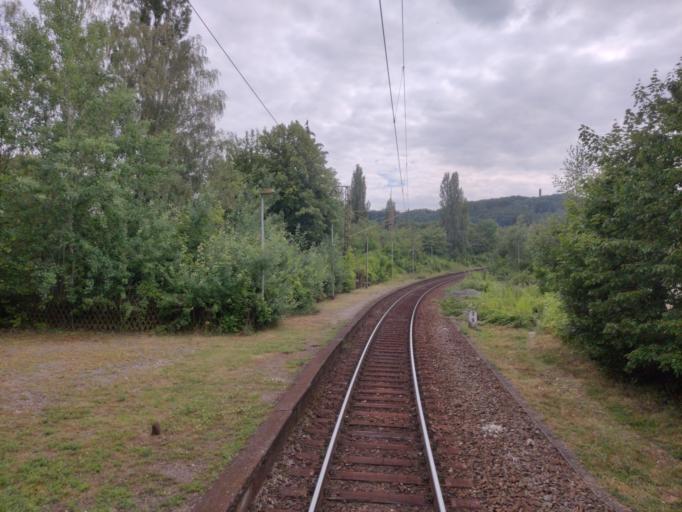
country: DE
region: Saxony-Anhalt
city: Blankenburg
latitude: 51.7970
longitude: 10.9422
